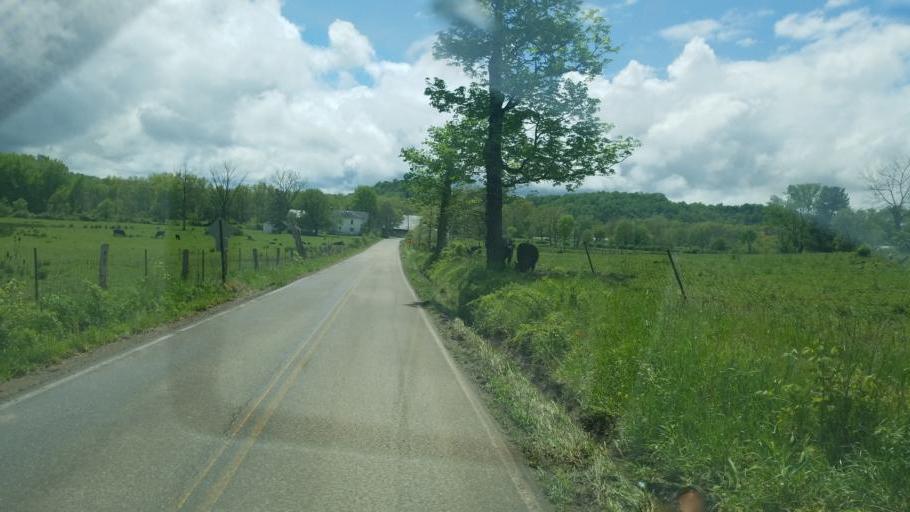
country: US
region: Ohio
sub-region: Tuscarawas County
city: Dennison
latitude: 40.3733
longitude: -81.2360
